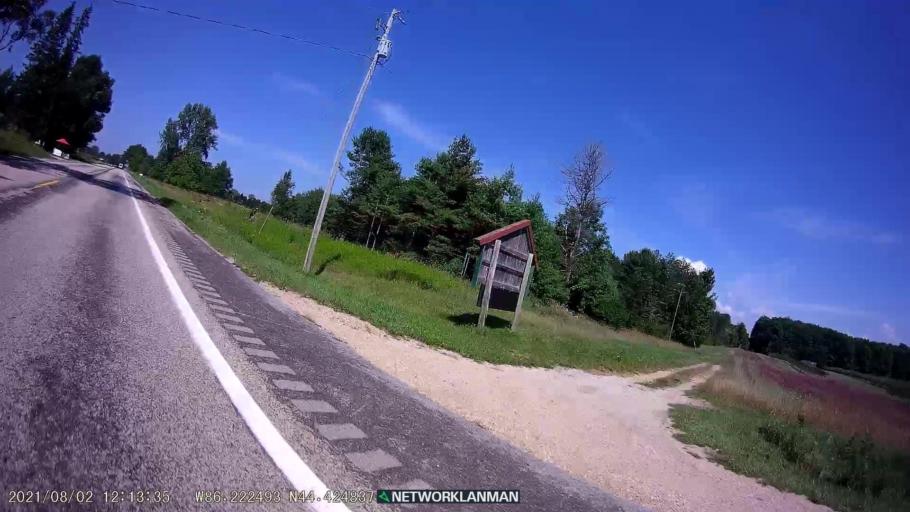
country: US
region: Michigan
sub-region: Manistee County
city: Manistee
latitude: 44.4251
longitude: -86.2225
